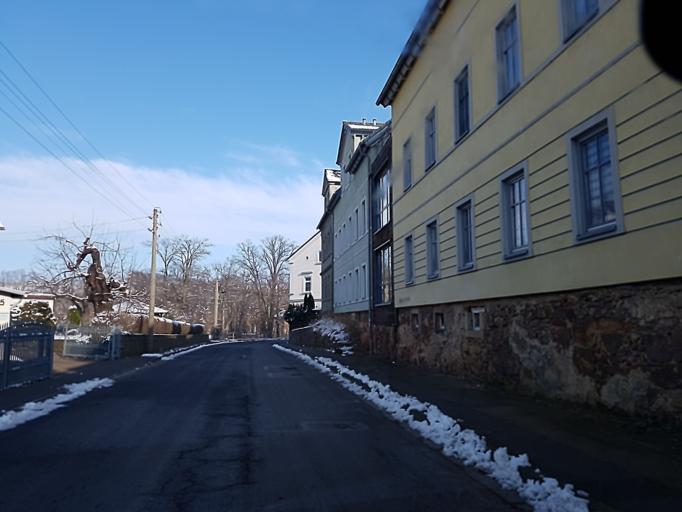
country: DE
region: Saxony
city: Leisnig
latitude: 51.1591
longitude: 12.9365
